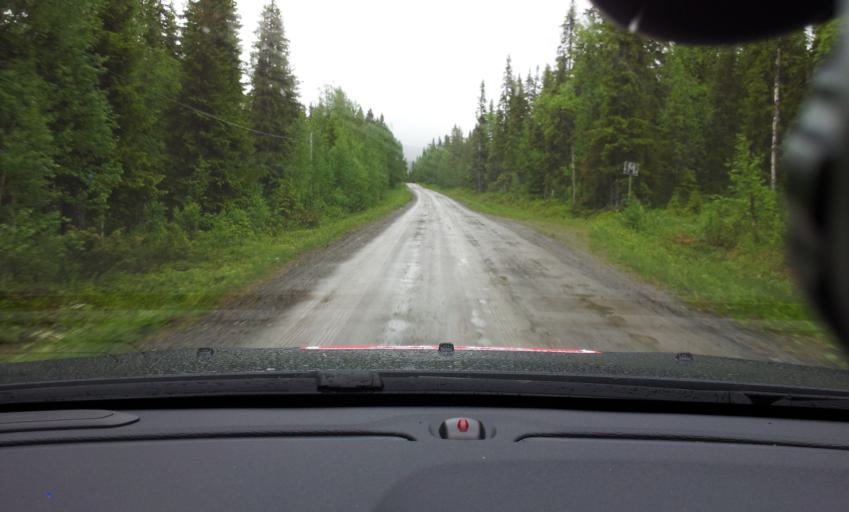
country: SE
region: Jaemtland
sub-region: Are Kommun
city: Are
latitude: 63.5086
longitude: 12.7026
